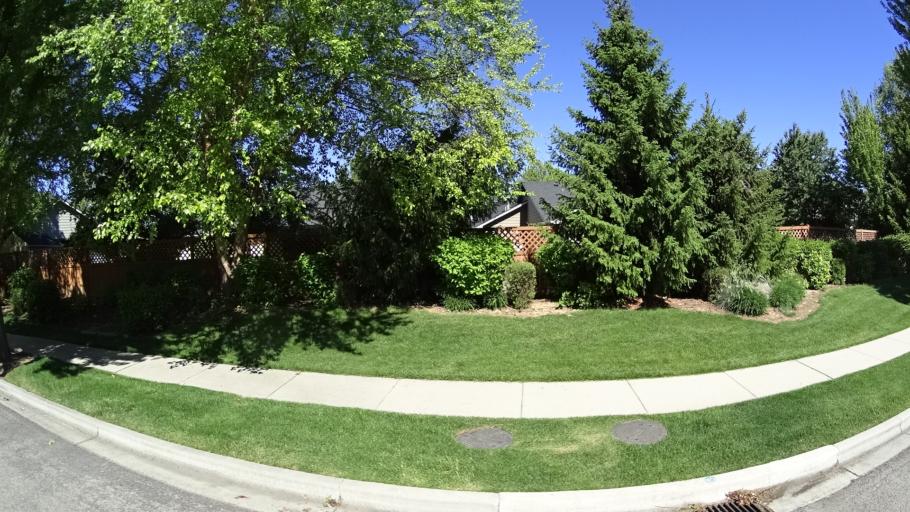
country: US
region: Idaho
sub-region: Ada County
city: Meridian
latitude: 43.6344
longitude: -116.3644
